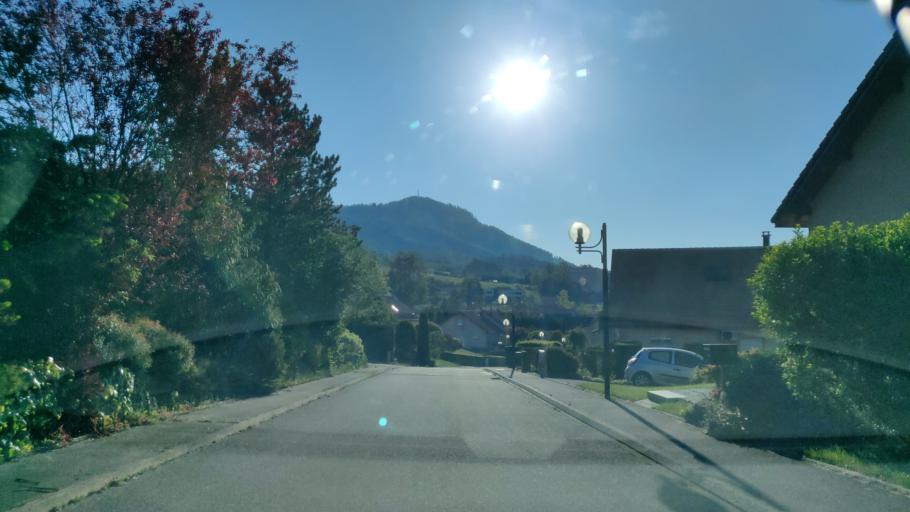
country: FR
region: Lorraine
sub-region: Departement des Vosges
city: Saint-Die-des-Vosges
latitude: 48.2956
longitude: 6.9565
